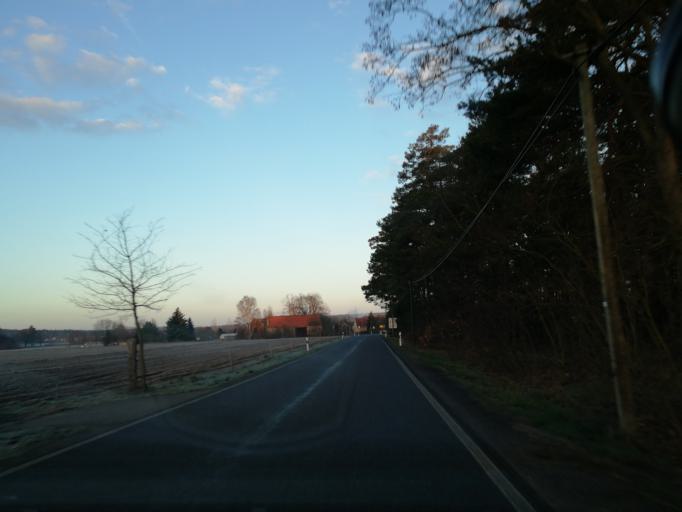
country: DE
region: Brandenburg
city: Crinitz
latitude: 51.7217
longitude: 13.8409
